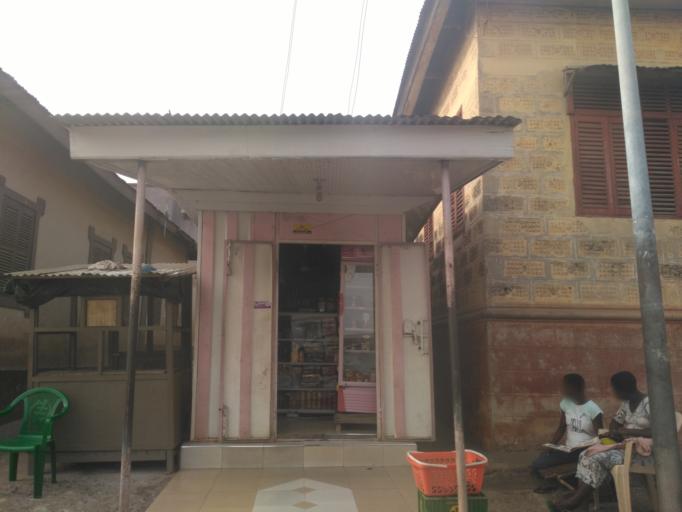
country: GH
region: Ashanti
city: Kumasi
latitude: 6.7043
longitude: -1.6217
